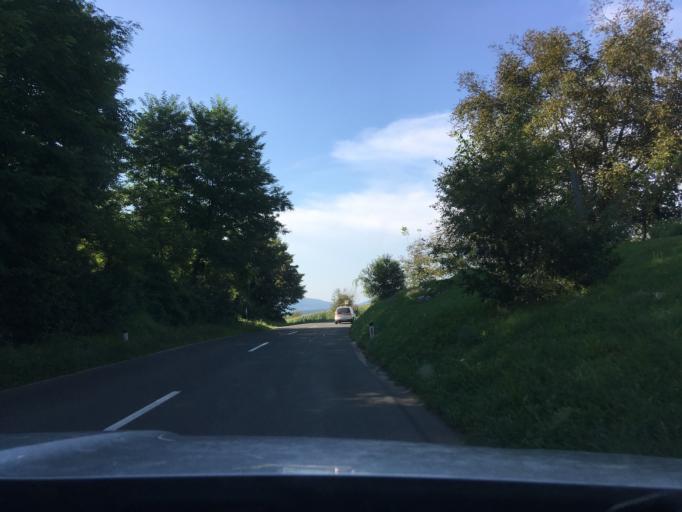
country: SI
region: Crnomelj
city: Crnomelj
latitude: 45.5088
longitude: 15.1864
